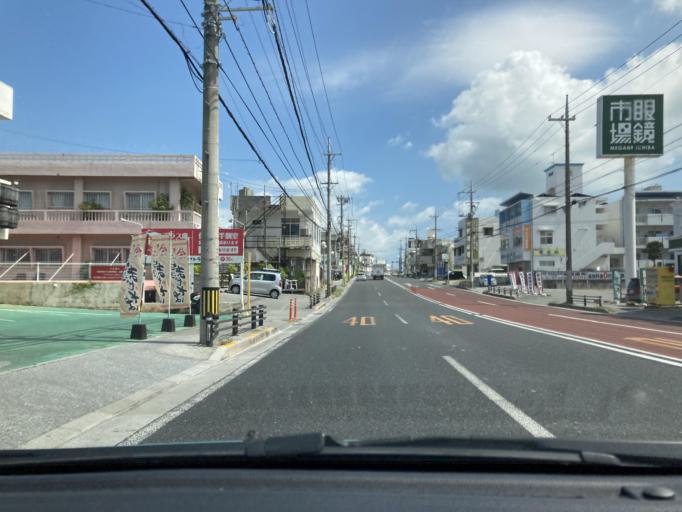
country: JP
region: Okinawa
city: Ginowan
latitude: 26.2730
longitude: 127.7723
